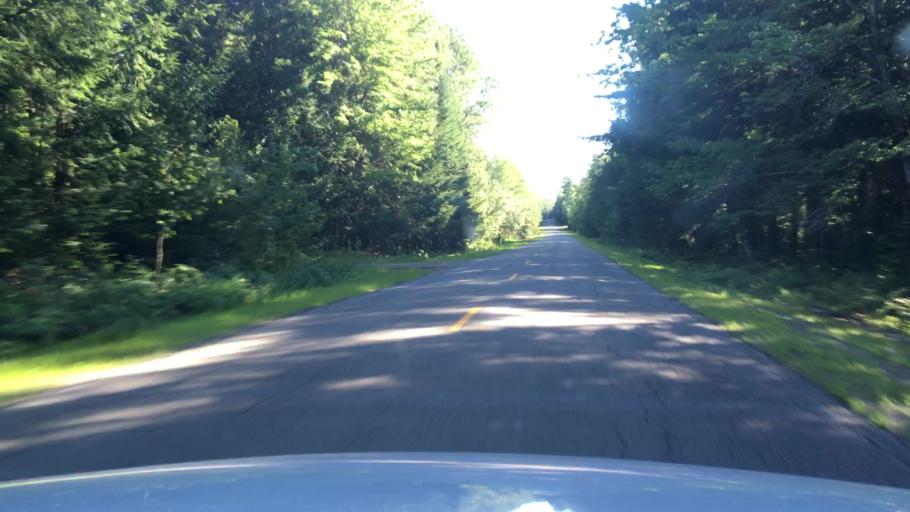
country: US
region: Maine
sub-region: Penobscot County
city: Enfield
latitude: 45.2184
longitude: -68.5829
